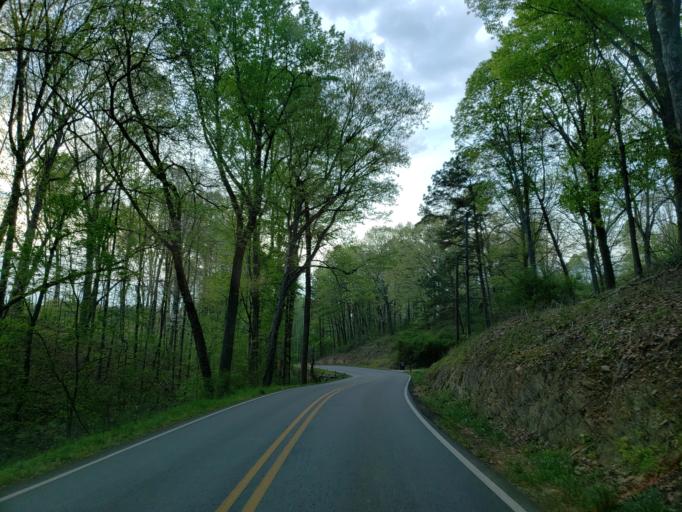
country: US
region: Georgia
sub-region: Cherokee County
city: Canton
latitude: 34.2897
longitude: -84.4577
